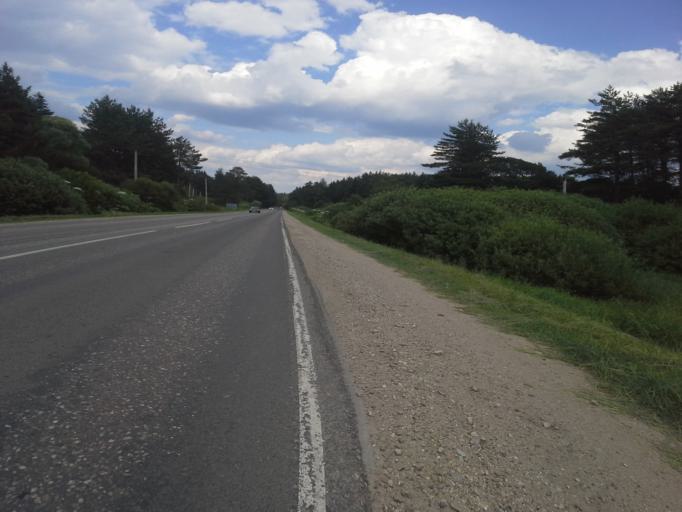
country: RU
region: Moskovskaya
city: Naro-Fominsk
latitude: 55.3991
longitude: 36.7774
